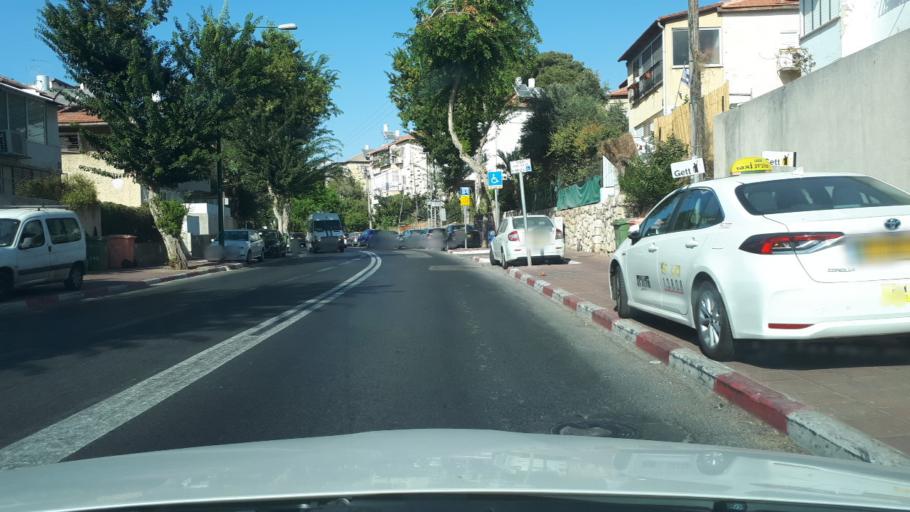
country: IL
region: Tel Aviv
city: Giv`atayim
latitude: 32.0628
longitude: 34.8231
